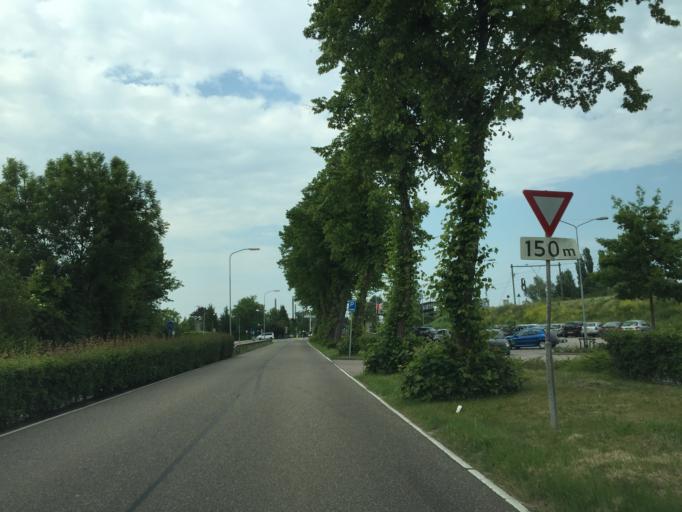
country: NL
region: Gelderland
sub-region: Gemeente Zaltbommel
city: Zaltbommel
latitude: 51.8058
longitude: 5.2631
